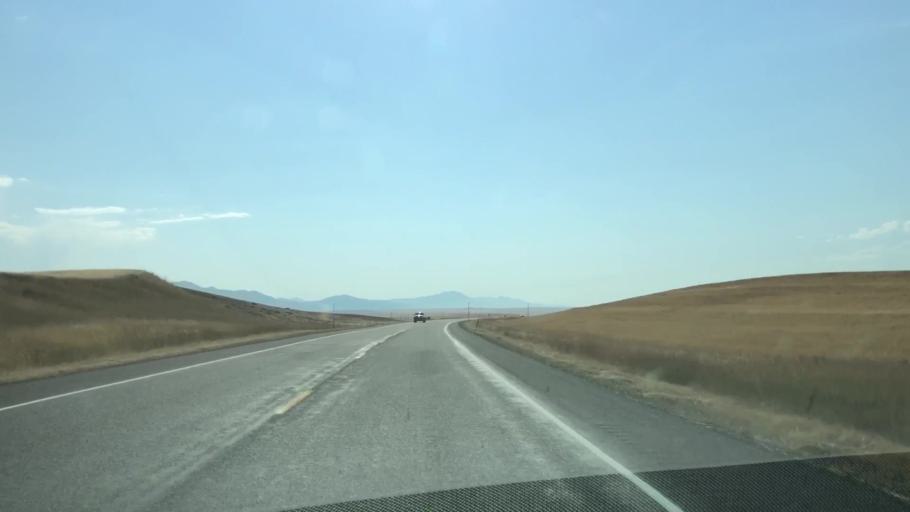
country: US
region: Idaho
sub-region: Madison County
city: Rexburg
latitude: 43.5834
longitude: -111.5756
